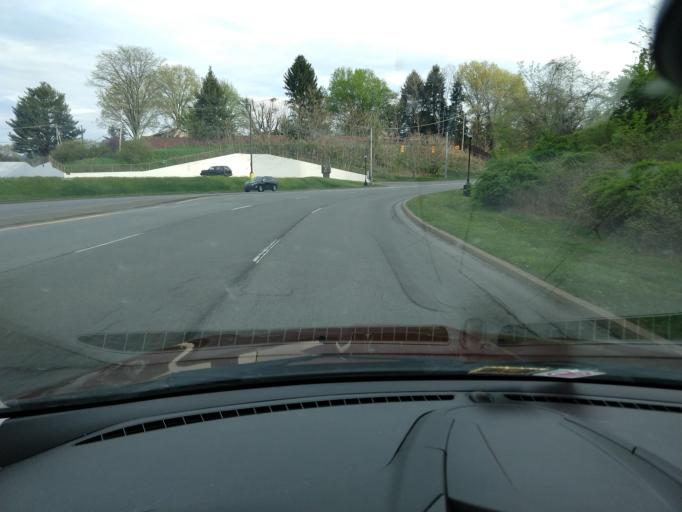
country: US
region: West Virginia
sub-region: Harrison County
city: Bridgeport
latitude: 39.3099
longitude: -80.2771
